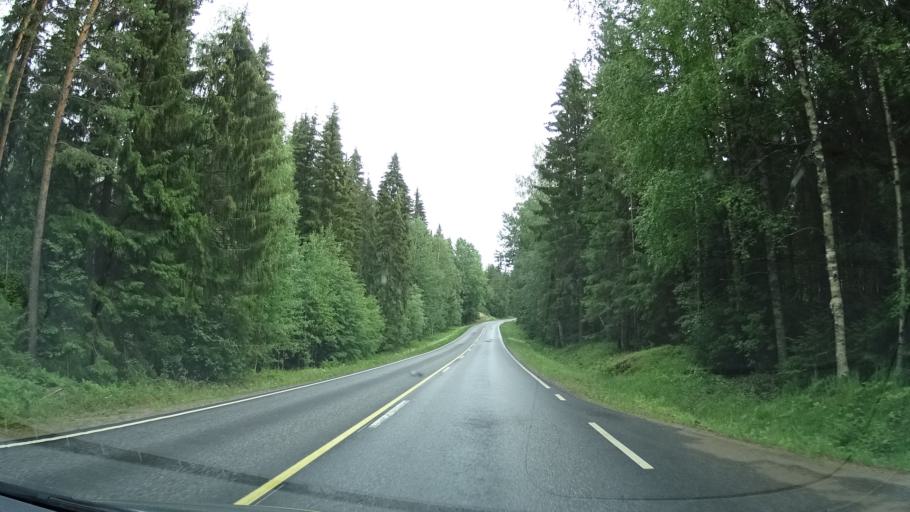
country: FI
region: Haeme
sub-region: Forssa
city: Humppila
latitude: 61.0975
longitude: 23.3417
